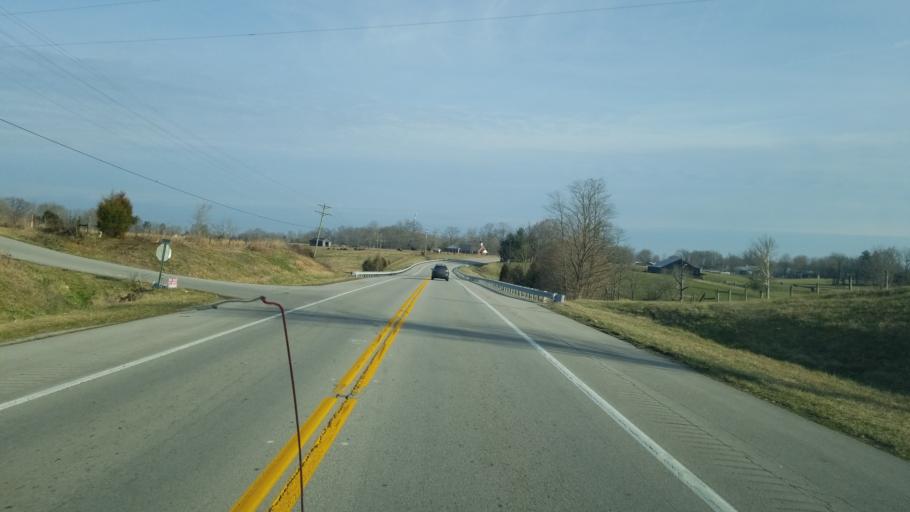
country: US
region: Kentucky
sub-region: Russell County
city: Russell Springs
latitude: 37.1174
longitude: -85.0483
